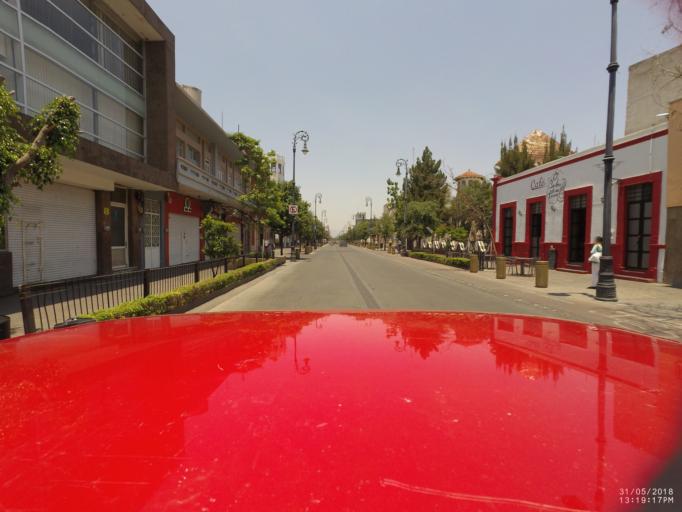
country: MX
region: Aguascalientes
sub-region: Aguascalientes
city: Aguascalientes
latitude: 21.8826
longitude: -102.2904
